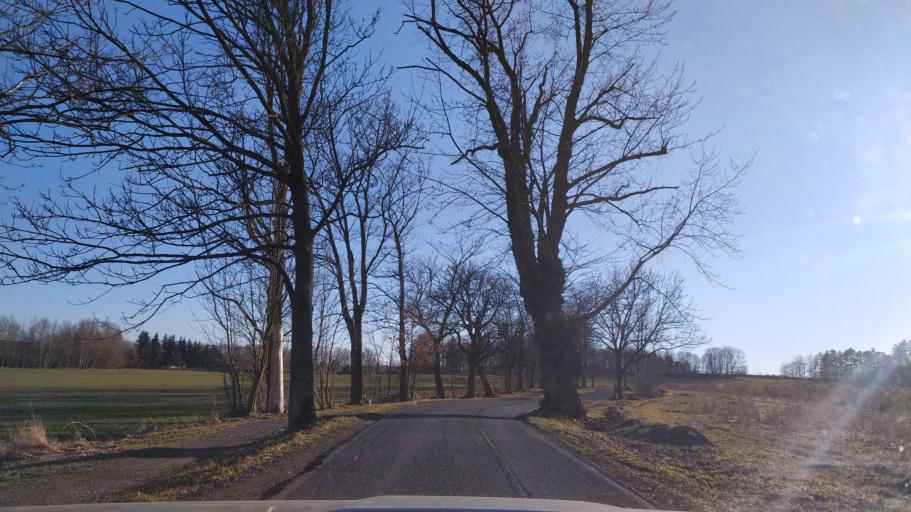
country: CZ
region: Karlovarsky
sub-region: Okres Cheb
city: Frantiskovy Lazne
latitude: 50.1035
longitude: 12.3443
